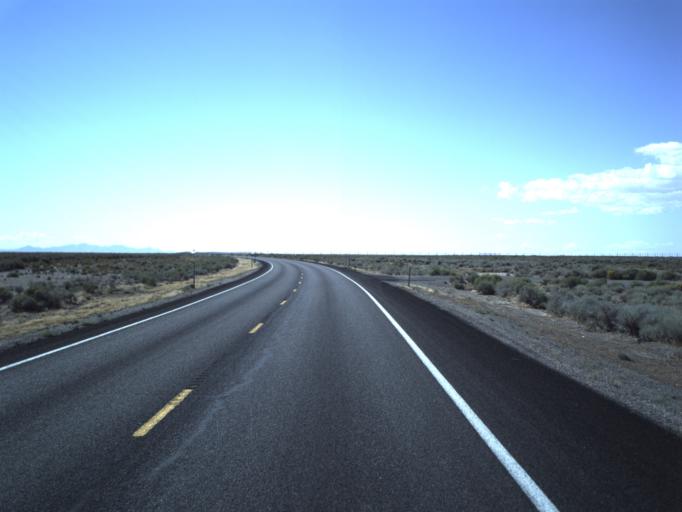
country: US
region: Utah
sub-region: Beaver County
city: Milford
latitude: 38.4454
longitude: -113.0091
